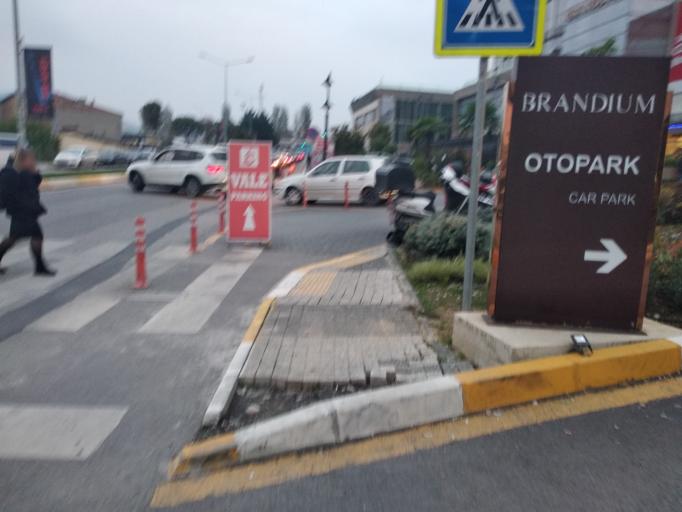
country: TR
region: Istanbul
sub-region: Atasehir
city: Atasehir
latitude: 40.9837
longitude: 29.1330
